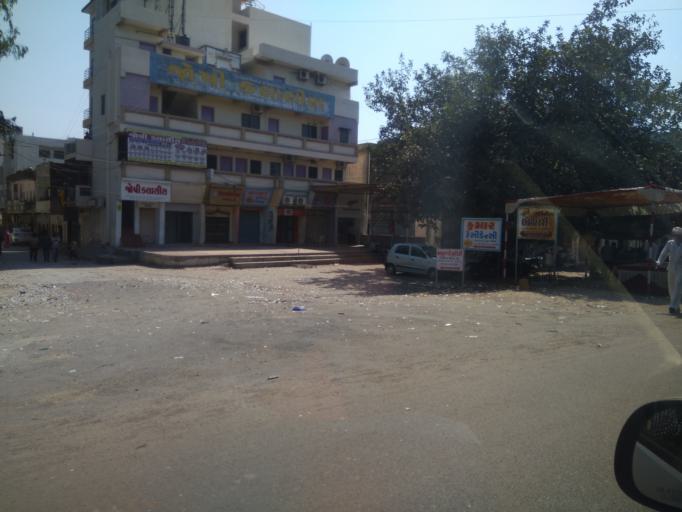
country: IN
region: Gujarat
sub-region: Jamnagar
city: Jamnagar
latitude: 22.4454
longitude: 70.0658
